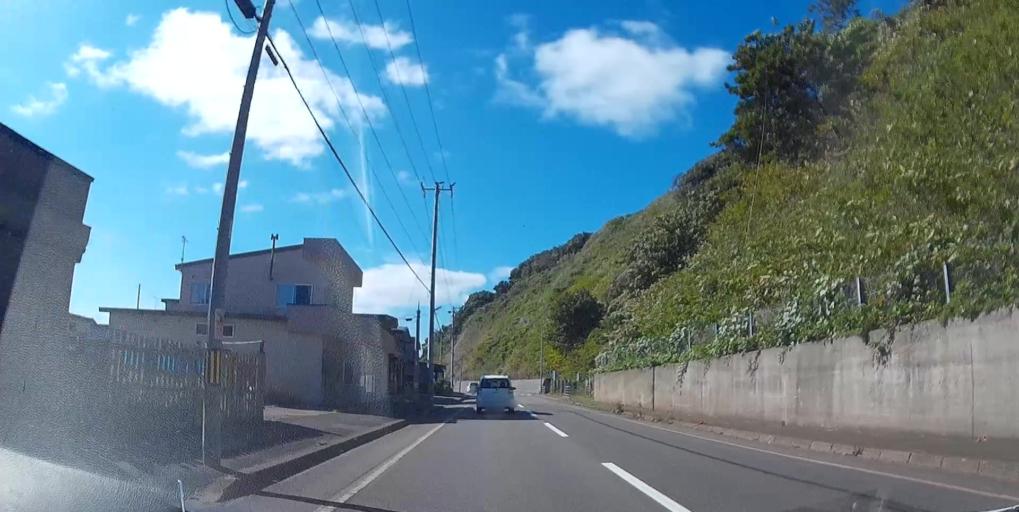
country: JP
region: Hokkaido
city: Kamiiso
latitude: 42.0487
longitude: 140.0805
